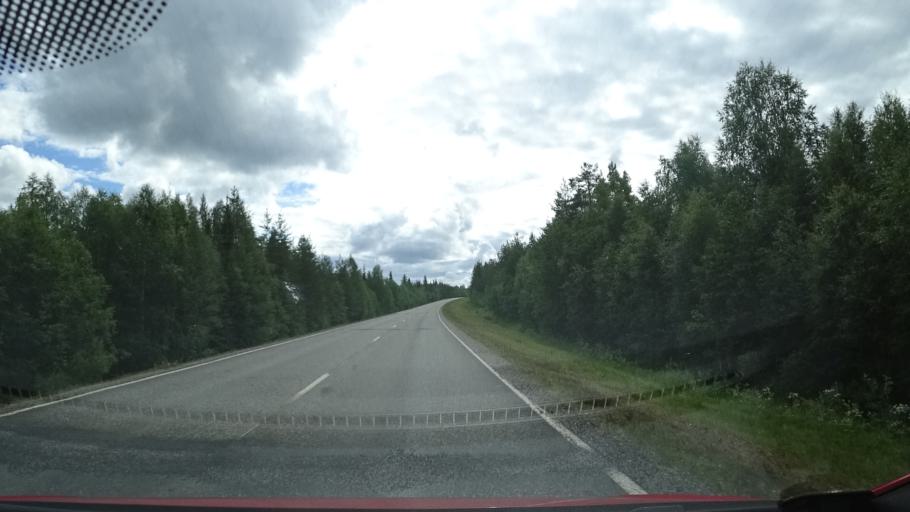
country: FI
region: Lapland
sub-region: Tunturi-Lappi
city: Kittilae
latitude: 67.5607
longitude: 24.9218
